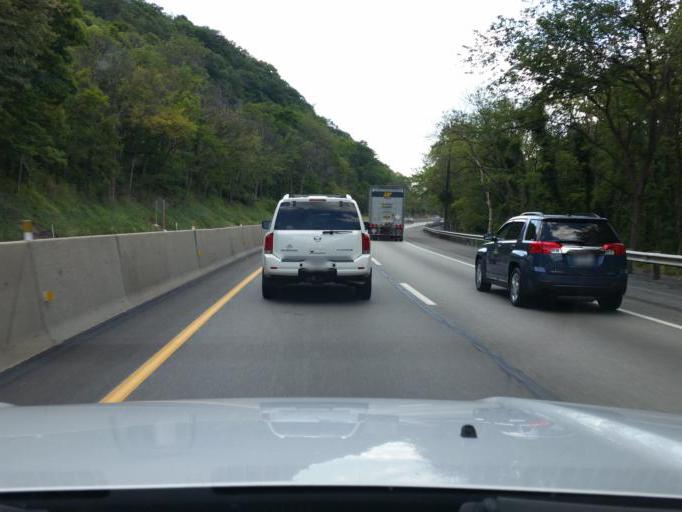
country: US
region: Pennsylvania
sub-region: Bedford County
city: Everett
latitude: 40.0108
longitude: -78.3959
